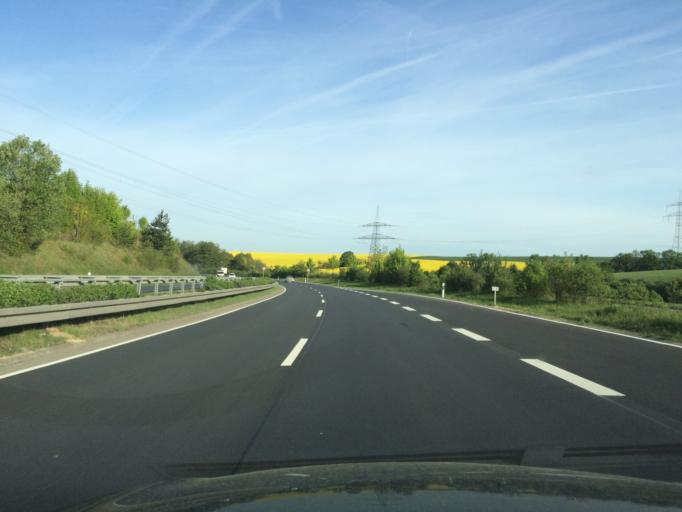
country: DE
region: Bavaria
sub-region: Regierungsbezirk Unterfranken
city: Rottendorf
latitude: 49.7800
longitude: 10.0513
